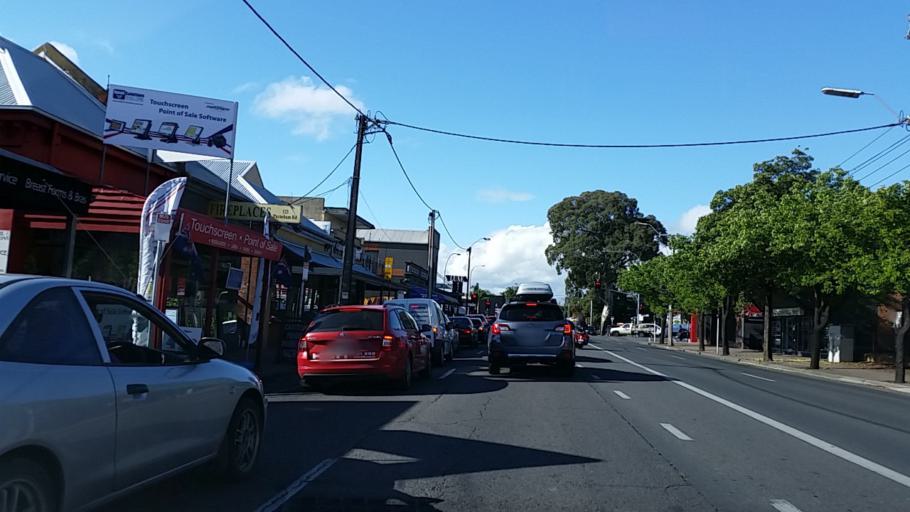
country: AU
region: South Australia
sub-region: Norwood Payneham St Peters
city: Royston Park
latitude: -34.9101
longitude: 138.6274
